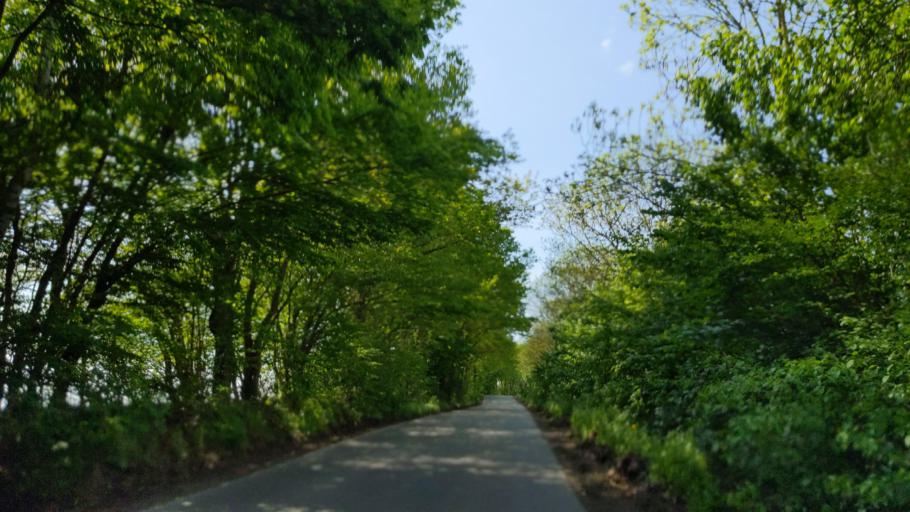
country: DE
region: Mecklenburg-Vorpommern
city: Selmsdorf
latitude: 53.8713
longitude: 10.8293
